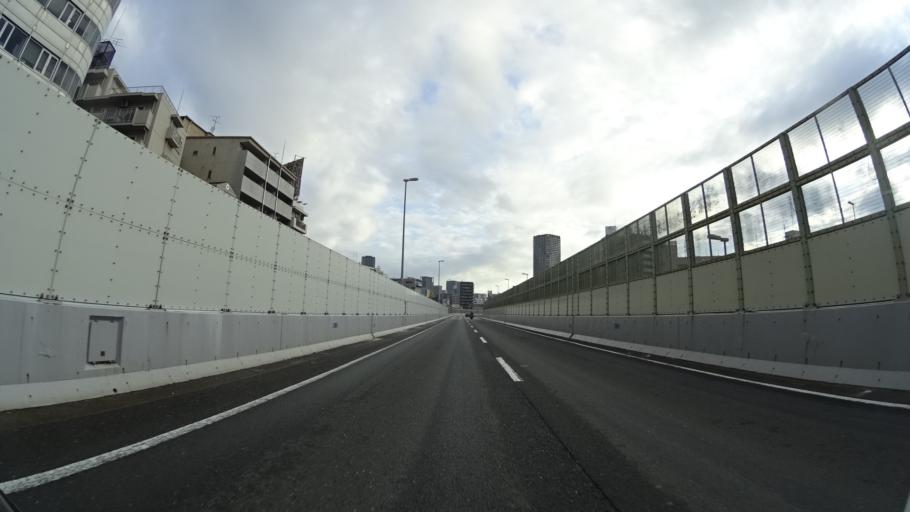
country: JP
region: Osaka
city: Osaka-shi
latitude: 34.6778
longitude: 135.4764
